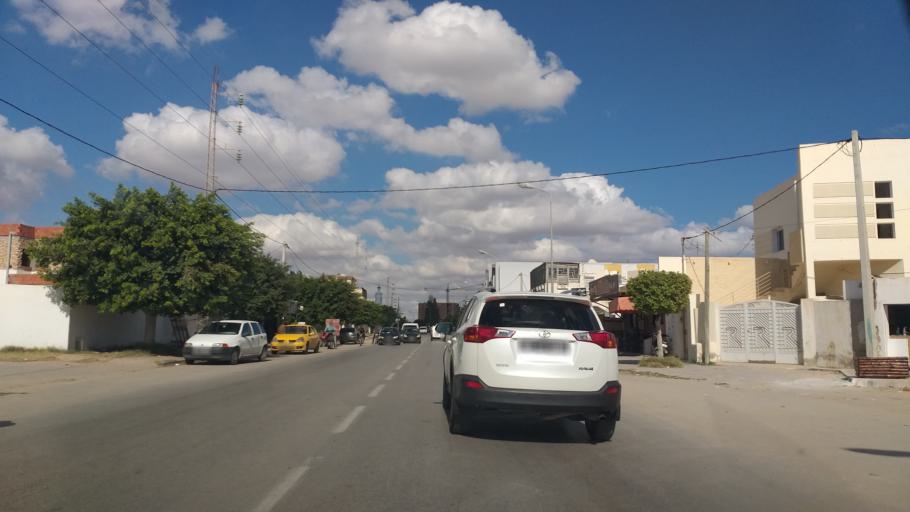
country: TN
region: Safaqis
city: Al Qarmadah
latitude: 34.7755
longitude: 10.7767
